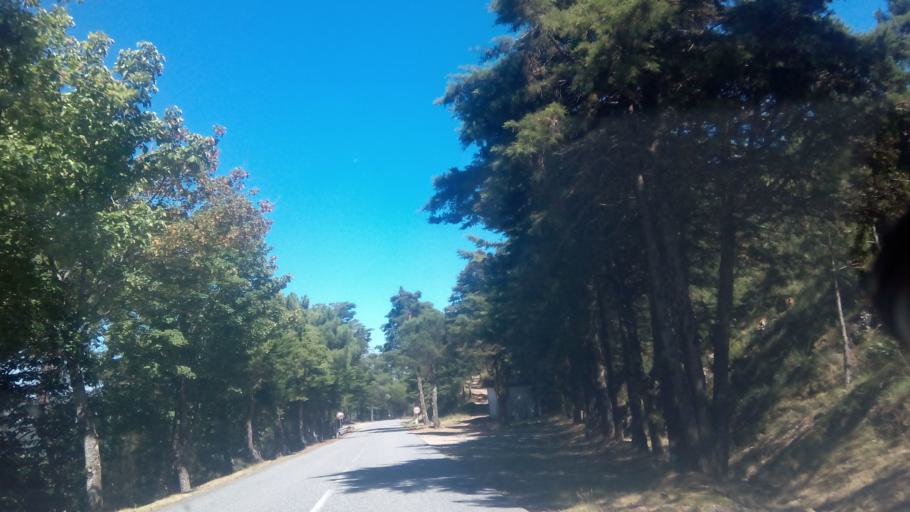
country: PT
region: Vila Real
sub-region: Santa Marta de Penaguiao
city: Santa Marta de Penaguiao
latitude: 41.2809
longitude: -7.8770
